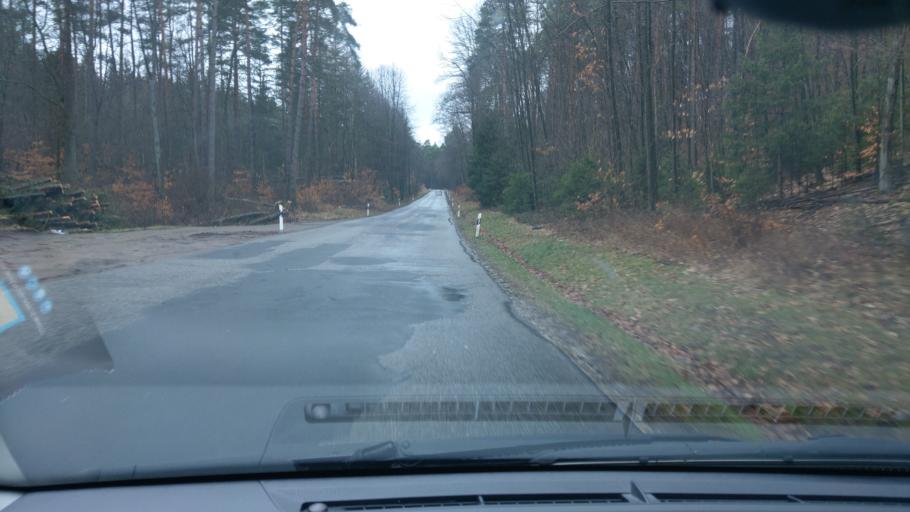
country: DE
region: Rheinland-Pfalz
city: Bechhofen
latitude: 49.3526
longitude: 7.3861
